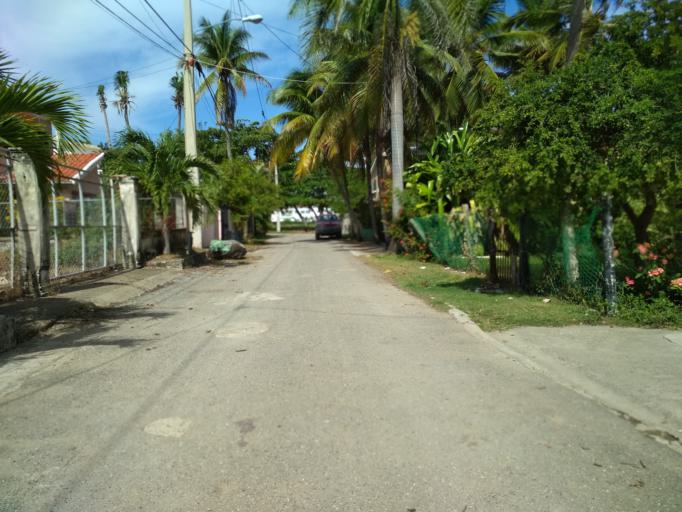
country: DO
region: Puerto Plata
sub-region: Puerto Plata
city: Puerto Plata
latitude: 19.8102
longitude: -70.7081
